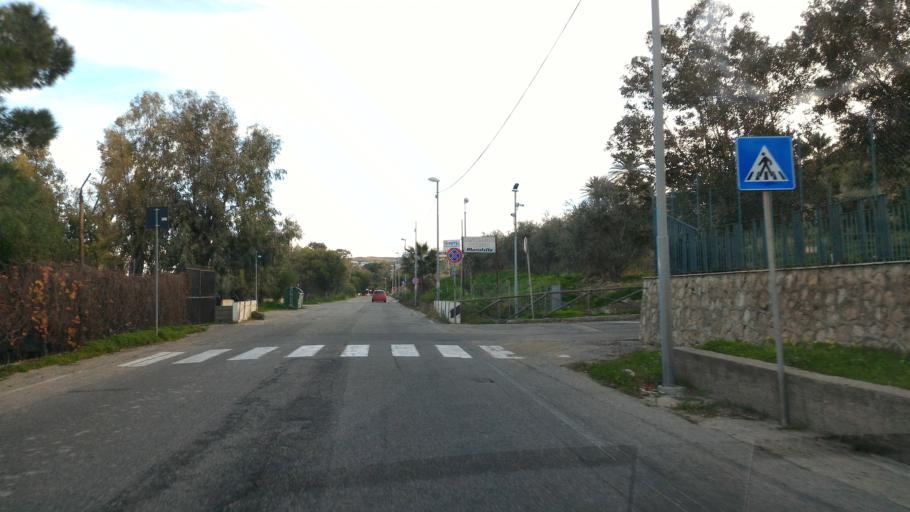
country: IT
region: Calabria
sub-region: Provincia di Crotone
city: Crotone
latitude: 39.0539
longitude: 17.1383
